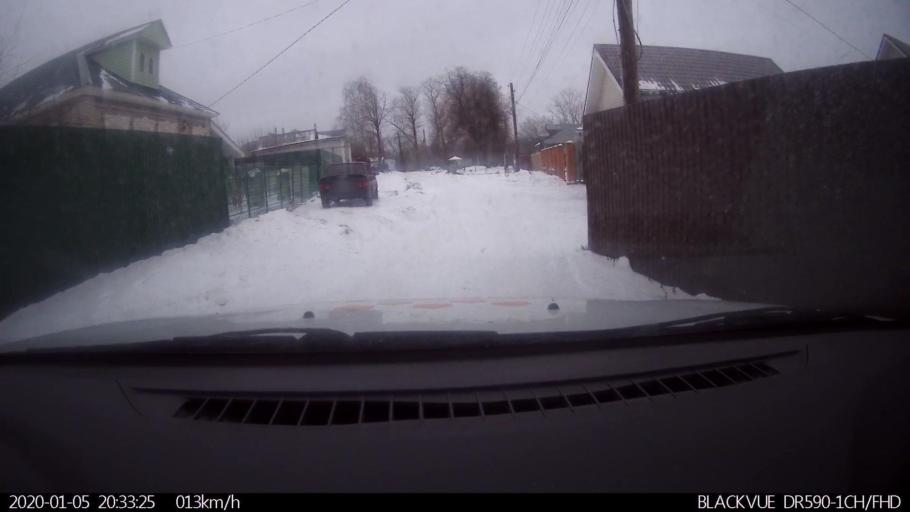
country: RU
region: Nizjnij Novgorod
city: Lukino
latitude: 56.4137
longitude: 43.7265
